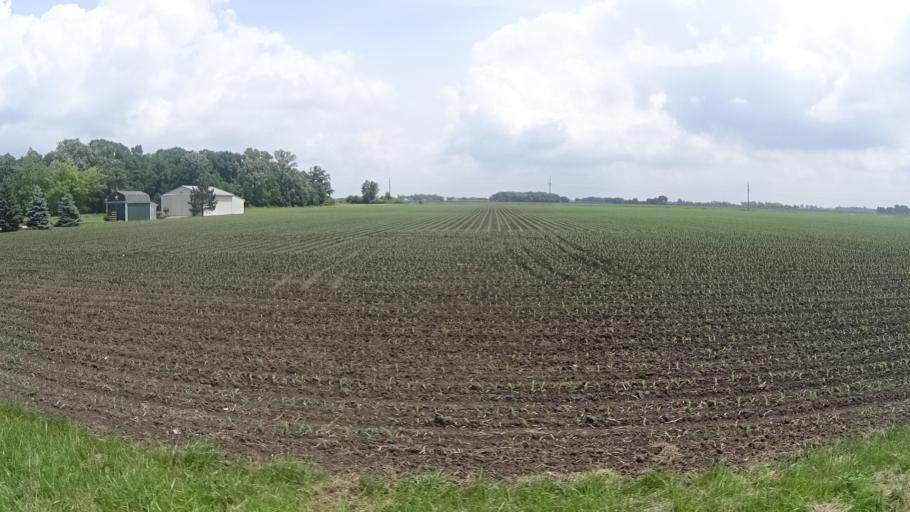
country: US
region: Ohio
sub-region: Huron County
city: Bellevue
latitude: 41.3217
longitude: -82.8053
